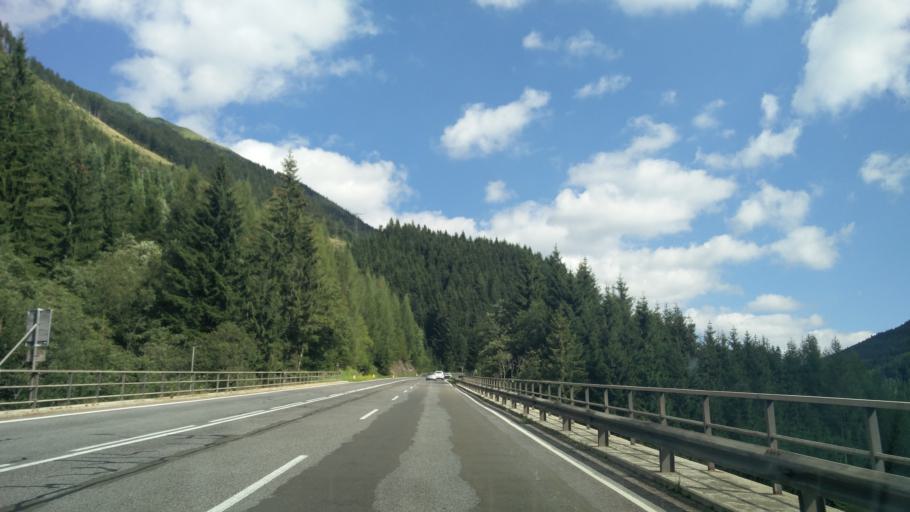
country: AT
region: Styria
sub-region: Politischer Bezirk Leoben
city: Eisenerz
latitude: 47.5359
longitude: 14.9317
